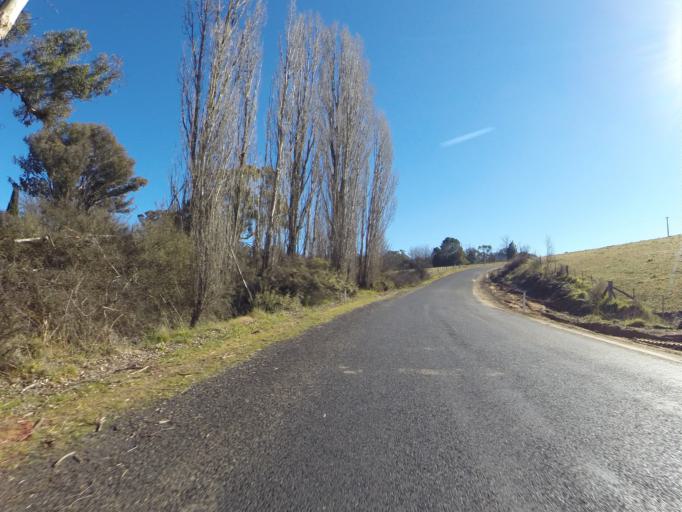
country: AU
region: New South Wales
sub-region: Oberon
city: Oberon
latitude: -33.5454
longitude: 149.8712
